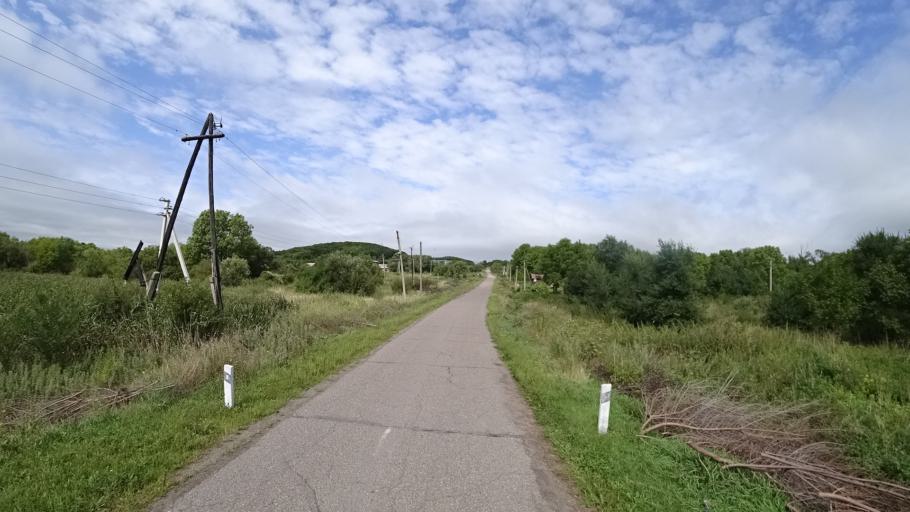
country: RU
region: Primorskiy
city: Lyalichi
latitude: 44.1362
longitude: 132.3875
